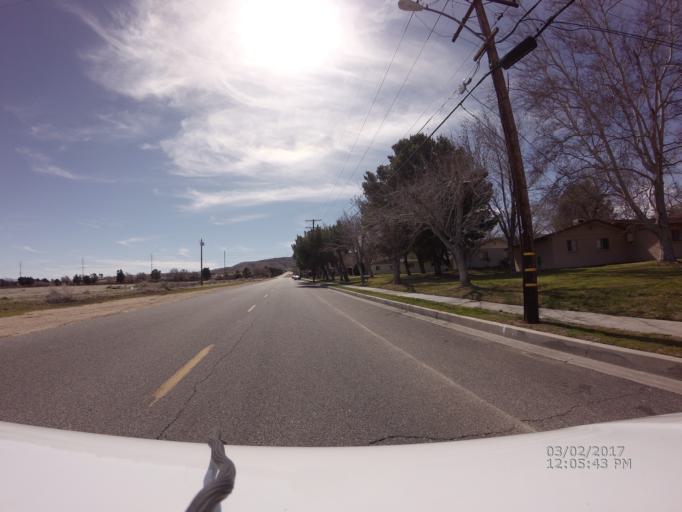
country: US
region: California
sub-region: Los Angeles County
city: Quartz Hill
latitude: 34.6476
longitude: -118.2450
